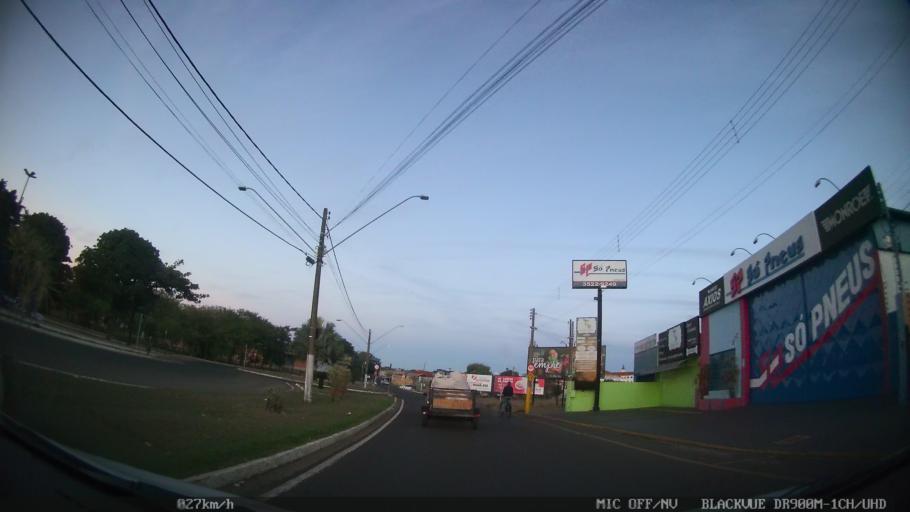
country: BR
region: Sao Paulo
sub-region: Catanduva
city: Catanduva
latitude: -21.1260
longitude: -48.9844
